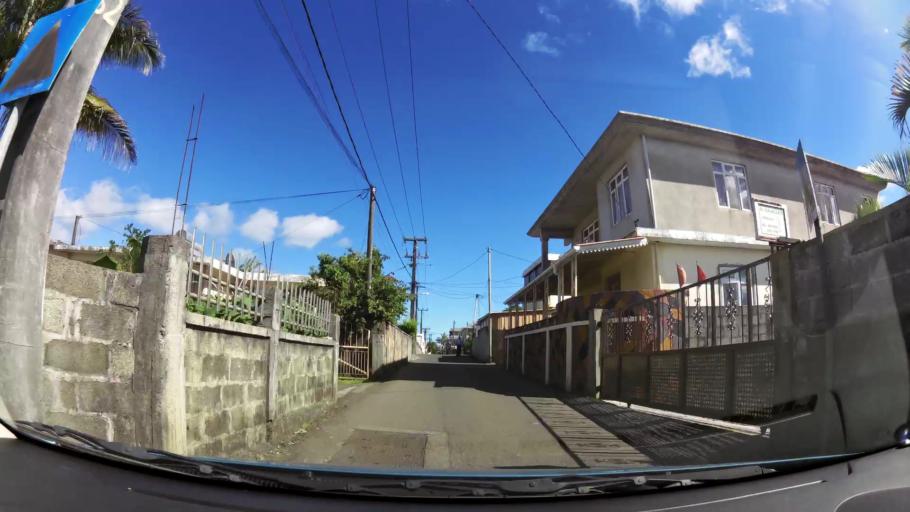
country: MU
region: Plaines Wilhems
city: Vacoas
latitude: -20.3189
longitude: 57.4857
